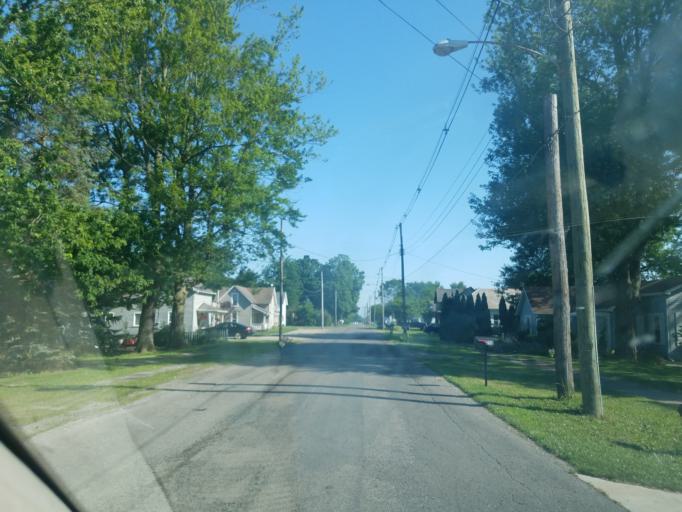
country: US
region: Ohio
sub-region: Union County
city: Richwood
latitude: 40.4303
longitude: -83.3021
